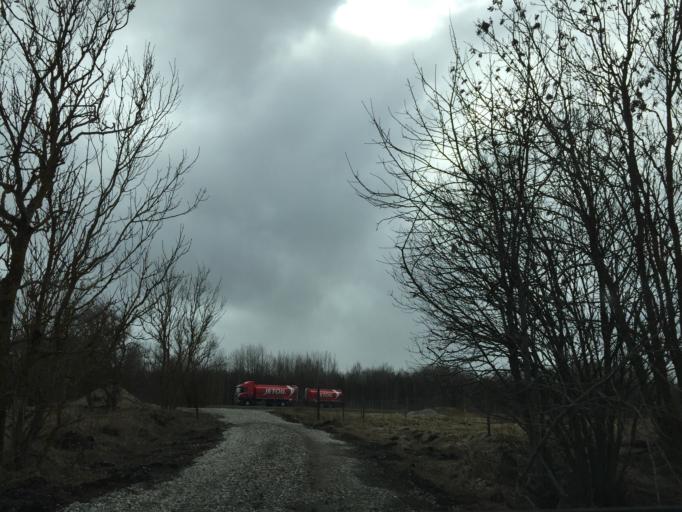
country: EE
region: Laeaene
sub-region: Lihula vald
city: Lihula
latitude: 58.7264
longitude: 23.9249
